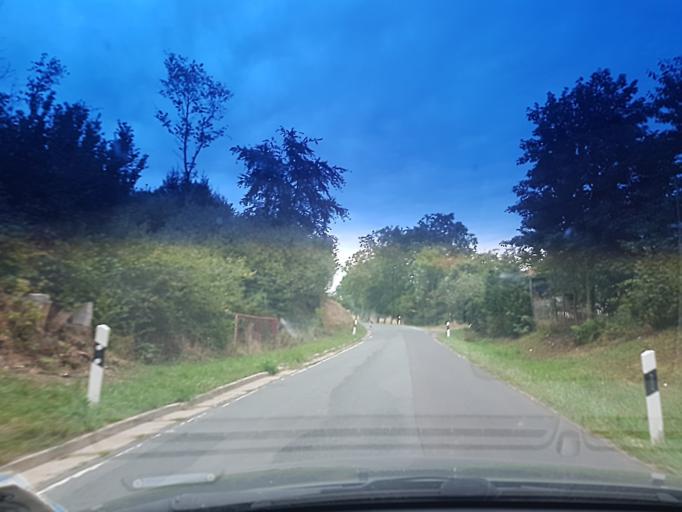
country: DE
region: Bavaria
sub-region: Regierungsbezirk Unterfranken
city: Geiselwind
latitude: 49.8006
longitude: 10.4912
